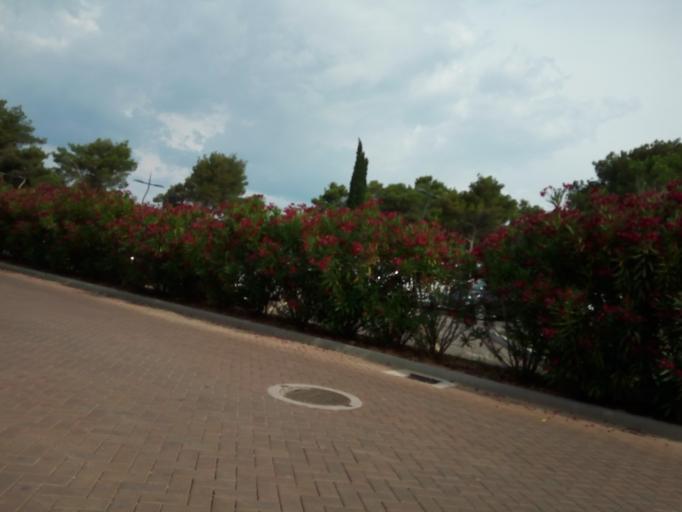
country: HR
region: Sibensko-Kniniska
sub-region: Grad Sibenik
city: Sibenik
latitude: 43.6968
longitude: 15.8878
